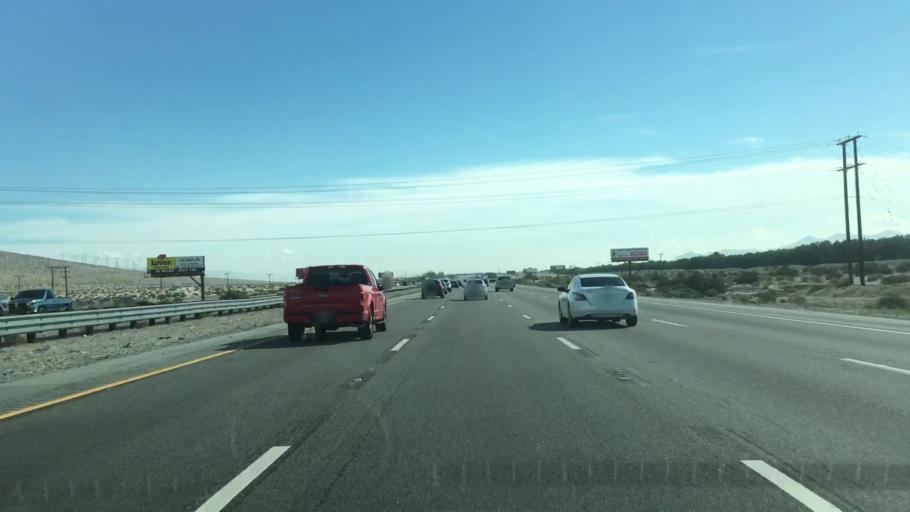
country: US
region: California
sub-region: Riverside County
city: Desert Edge
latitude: 33.8599
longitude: -116.4764
